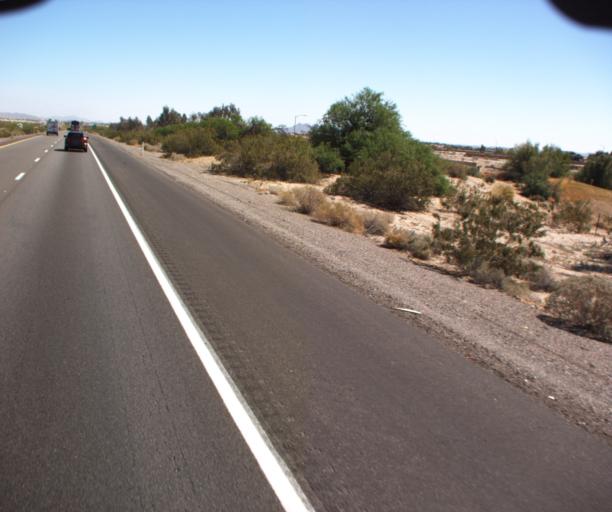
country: US
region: Arizona
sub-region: Yuma County
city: Wellton
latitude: 32.6549
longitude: -114.1710
